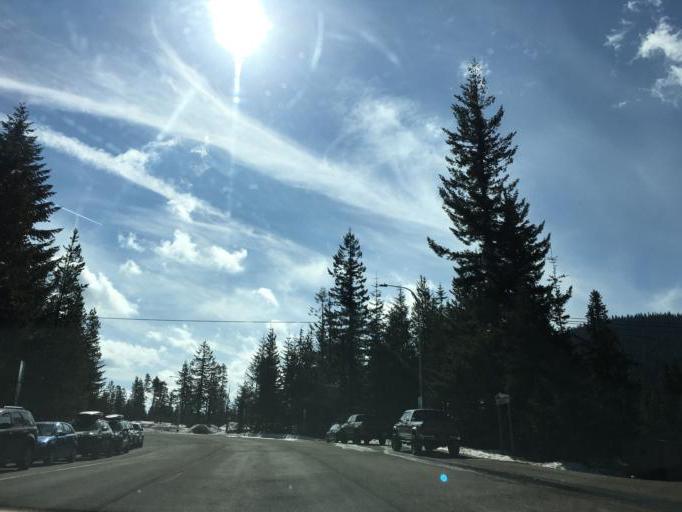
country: US
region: Oregon
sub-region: Clackamas County
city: Mount Hood Village
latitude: 45.3036
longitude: -121.7528
